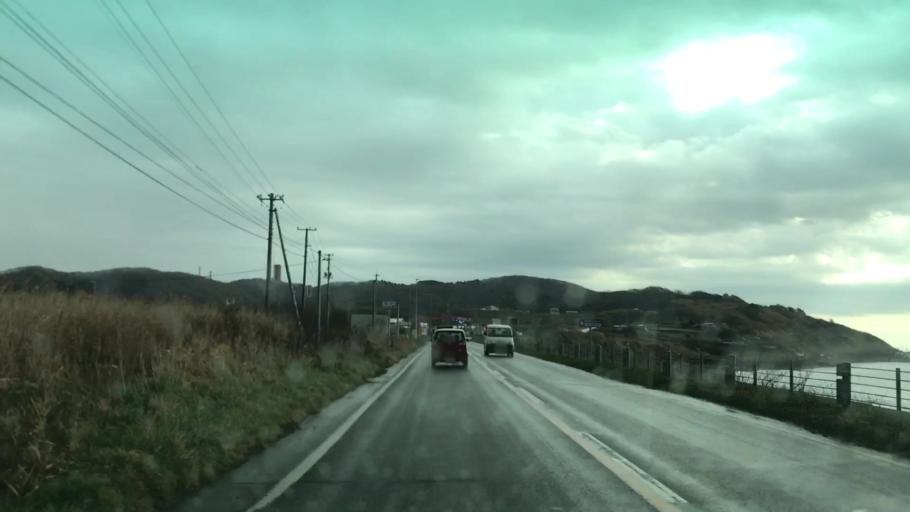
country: JP
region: Hokkaido
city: Shizunai-furukawacho
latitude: 42.1860
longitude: 142.7187
